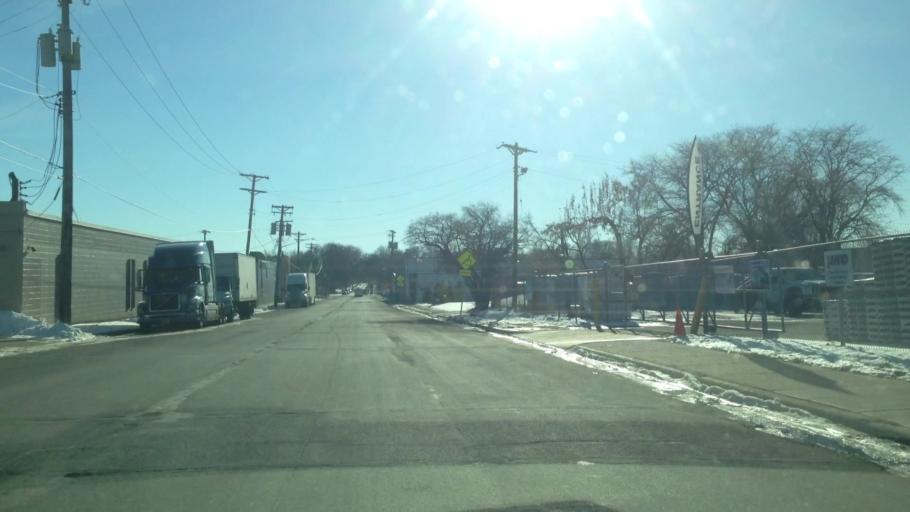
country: US
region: Minnesota
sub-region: Ramsey County
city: Lauderdale
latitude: 44.9947
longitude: -93.2178
